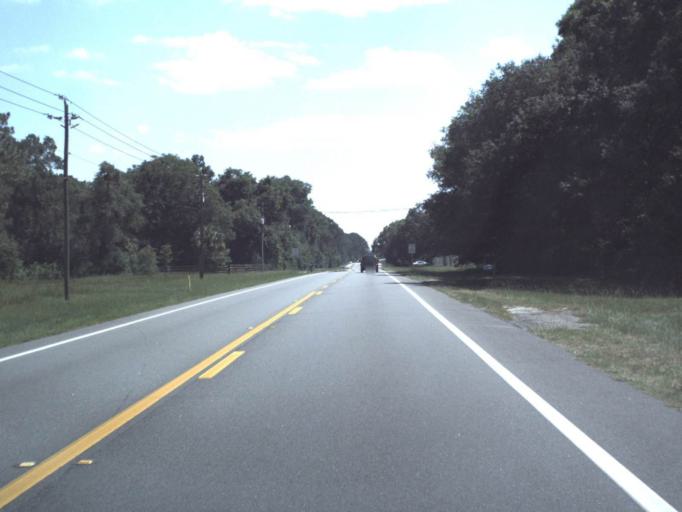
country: US
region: Florida
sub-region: Nassau County
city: Yulee
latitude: 30.5965
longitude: -81.5991
